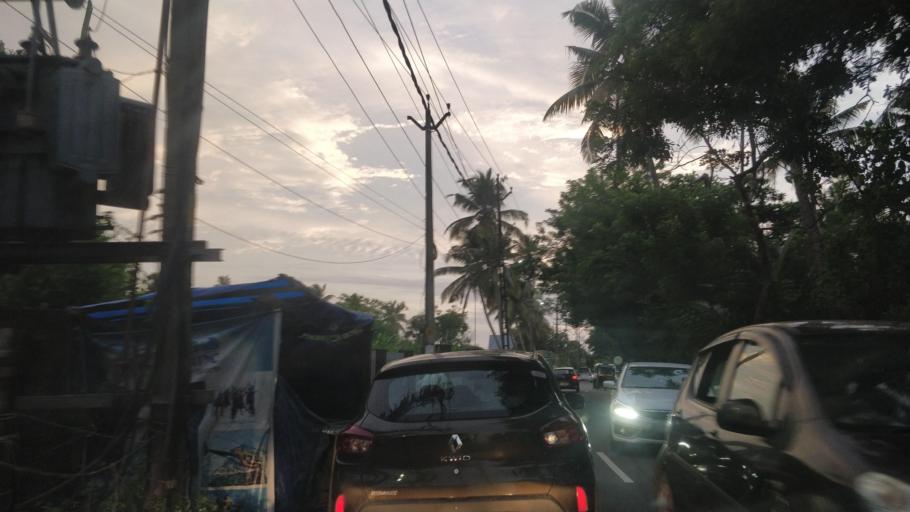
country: IN
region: Kerala
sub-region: Thrissur District
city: Kodungallur
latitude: 10.1405
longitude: 76.1865
